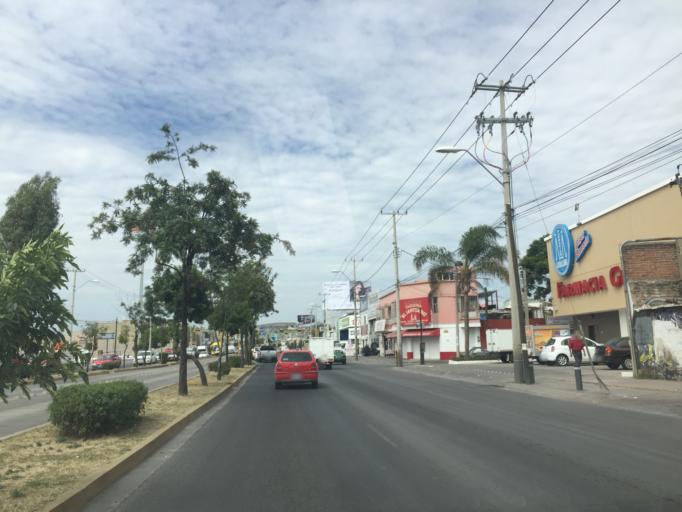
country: MX
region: Guanajuato
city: Leon
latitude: 21.1041
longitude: -101.6929
